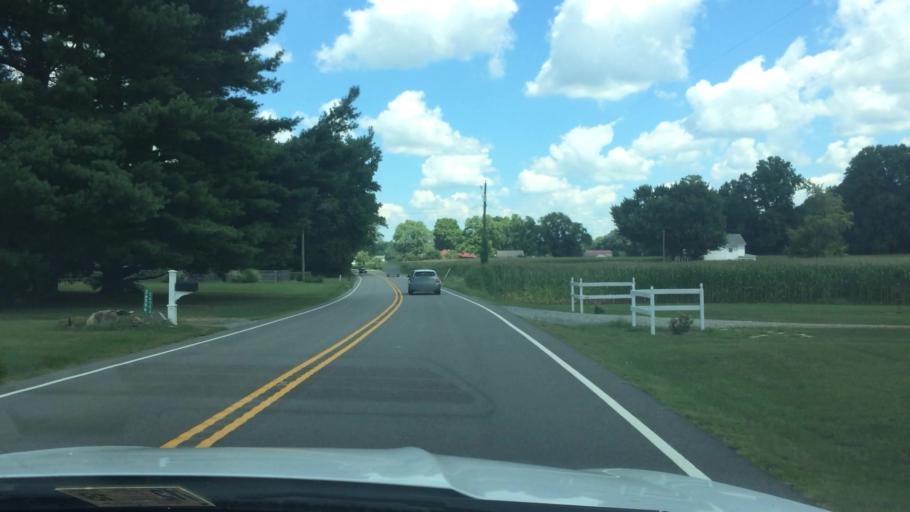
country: US
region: Virginia
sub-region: King William County
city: West Point
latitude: 37.5916
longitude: -76.7644
